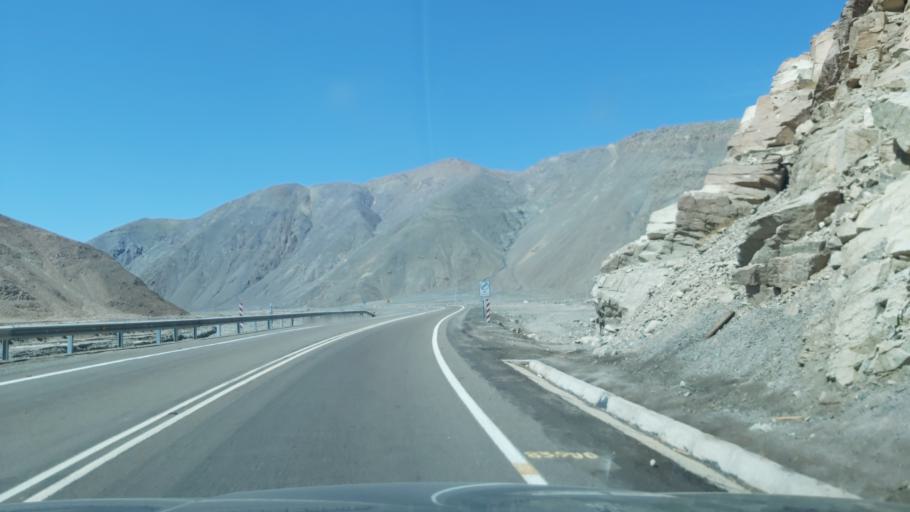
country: CL
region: Atacama
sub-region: Provincia de Chanaral
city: Diego de Almagro
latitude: -26.3388
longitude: -69.7462
